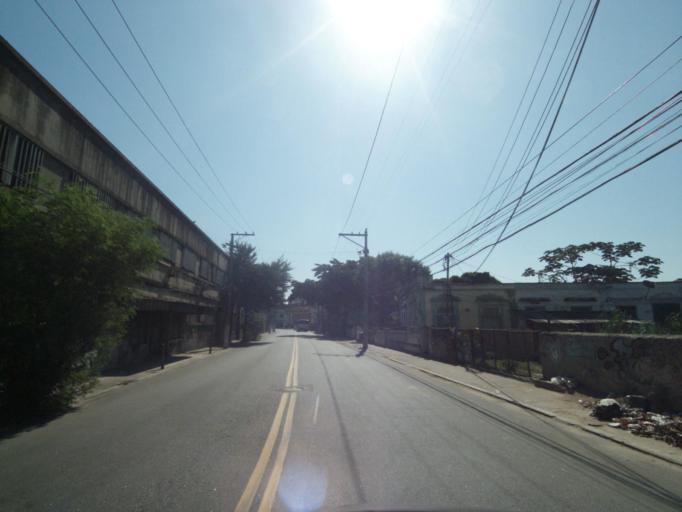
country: BR
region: Rio de Janeiro
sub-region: Niteroi
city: Niteroi
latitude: -22.8600
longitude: -43.0984
